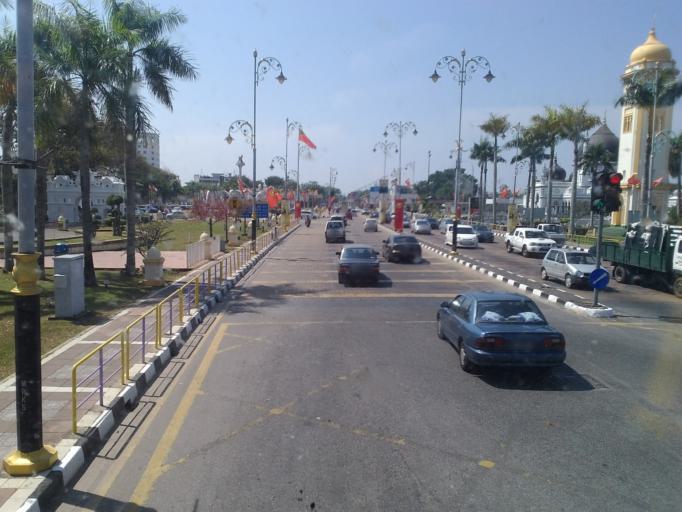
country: MY
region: Kedah
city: Alor Setar
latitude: 6.1215
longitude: 100.3665
